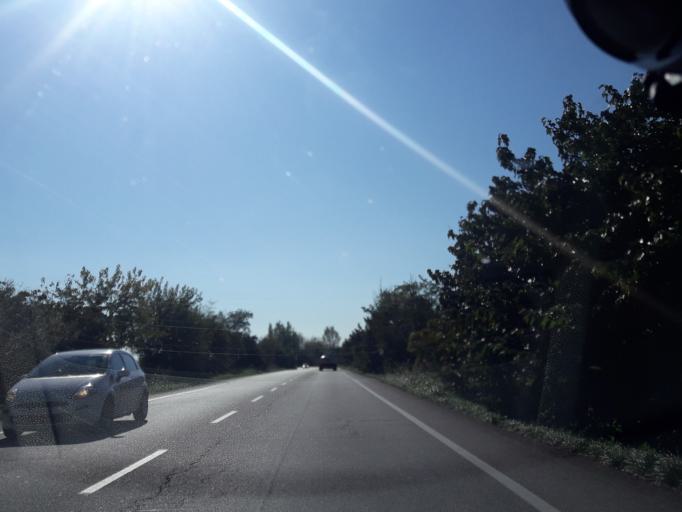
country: IT
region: Friuli Venezia Giulia
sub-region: Provincia di Udine
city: Povoletto
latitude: 46.1040
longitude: 13.2831
